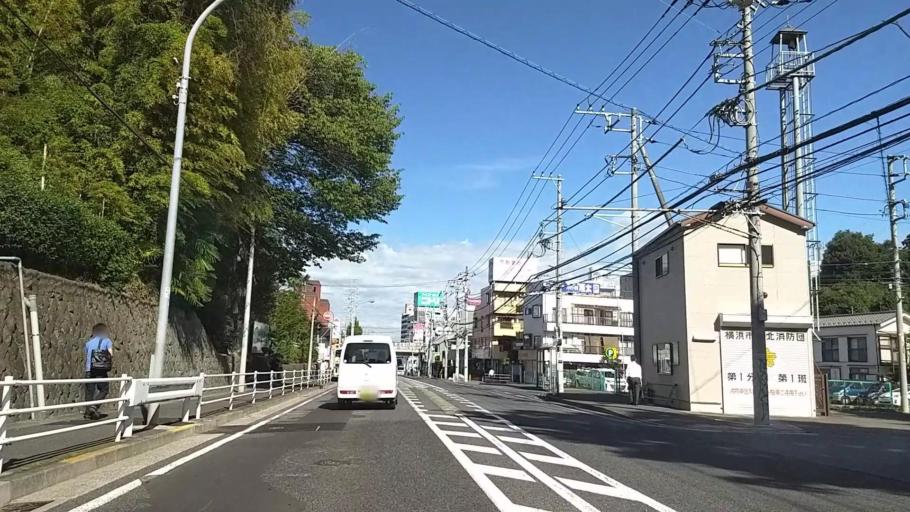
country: JP
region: Kanagawa
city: Yokohama
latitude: 35.4999
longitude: 139.6111
